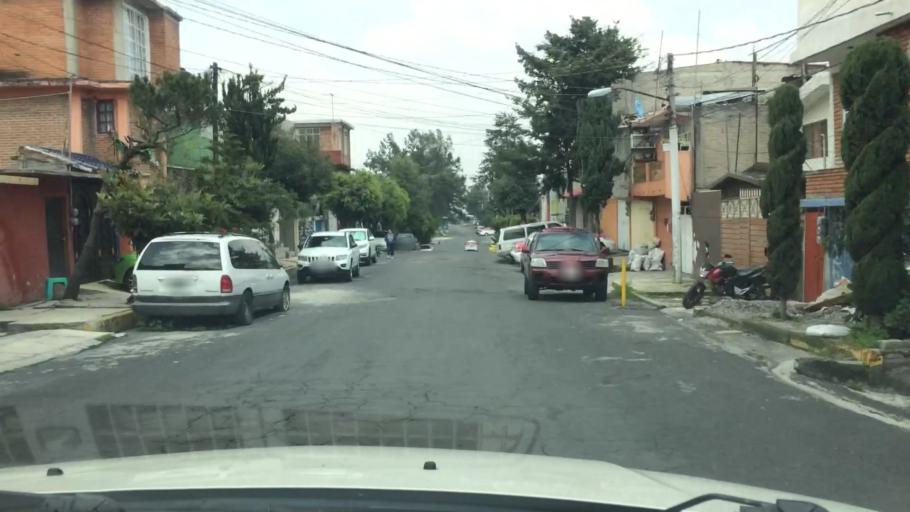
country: MX
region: Mexico City
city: Magdalena Contreras
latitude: 19.2906
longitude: -99.2249
